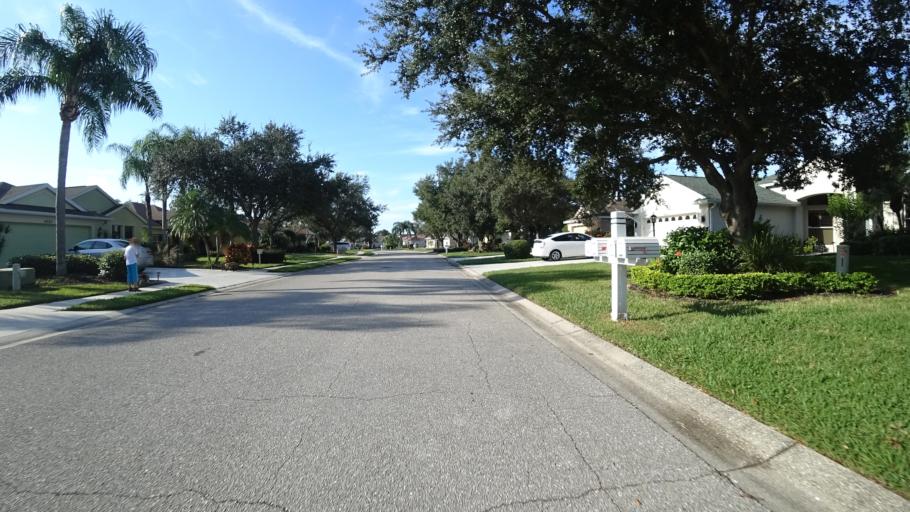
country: US
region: Florida
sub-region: Sarasota County
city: Desoto Lakes
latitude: 27.4229
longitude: -82.4960
